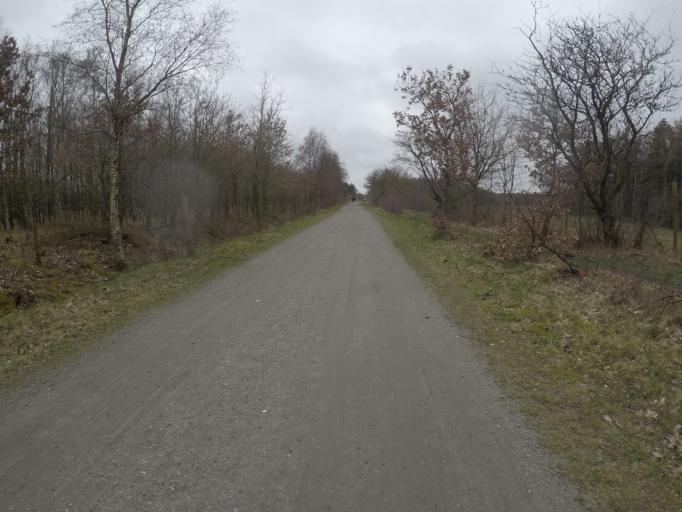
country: DE
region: Lower Saxony
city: Nordholz
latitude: 53.8339
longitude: 8.6250
